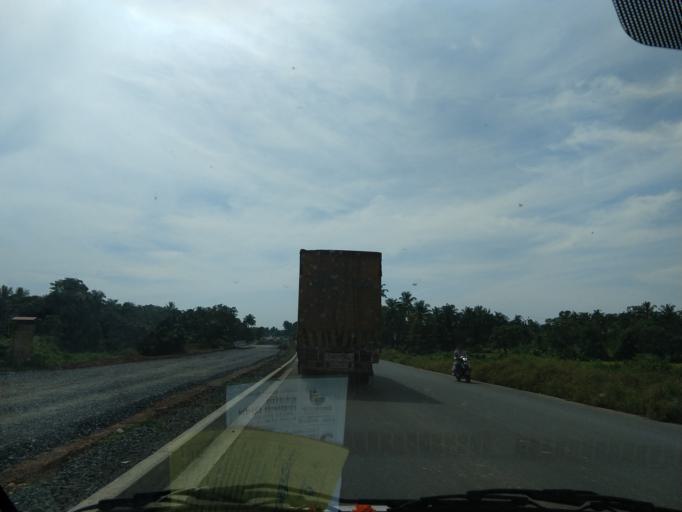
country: IN
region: Maharashtra
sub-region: Sindhudurg
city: Kudal
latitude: 15.9904
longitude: 73.6997
